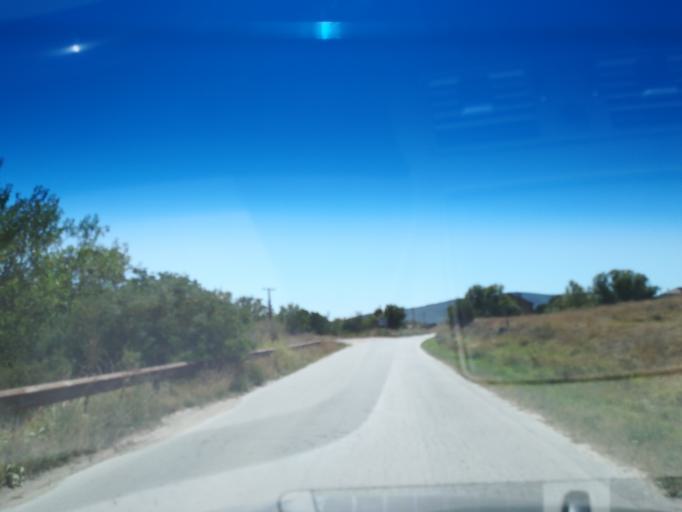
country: BG
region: Pazardzhik
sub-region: Obshtina Strelcha
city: Strelcha
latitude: 42.5171
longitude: 24.3223
